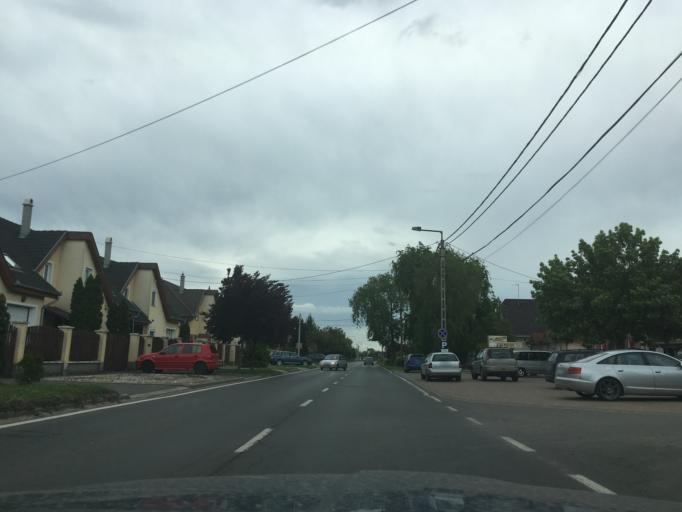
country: HU
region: Hajdu-Bihar
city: Debrecen
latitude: 47.5370
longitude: 21.6713
